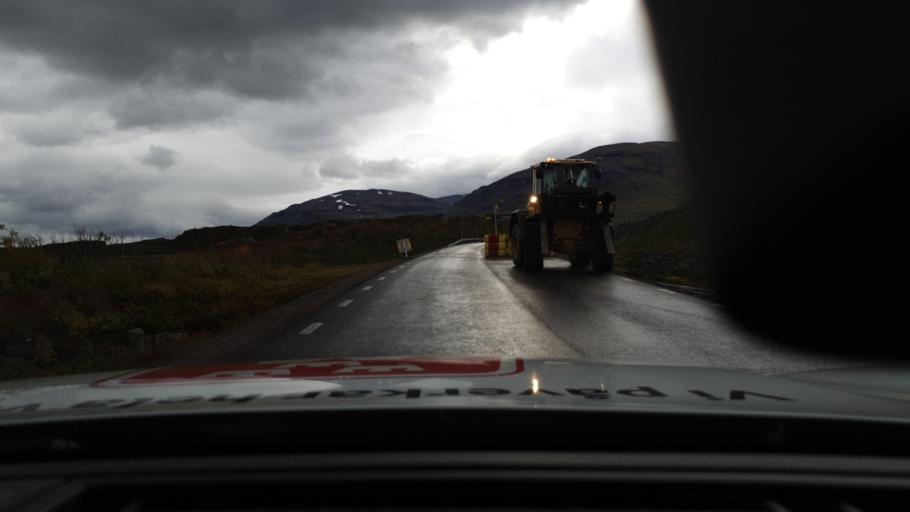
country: NO
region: Troms
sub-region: Bardu
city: Setermoen
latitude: 68.4338
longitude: 18.2579
